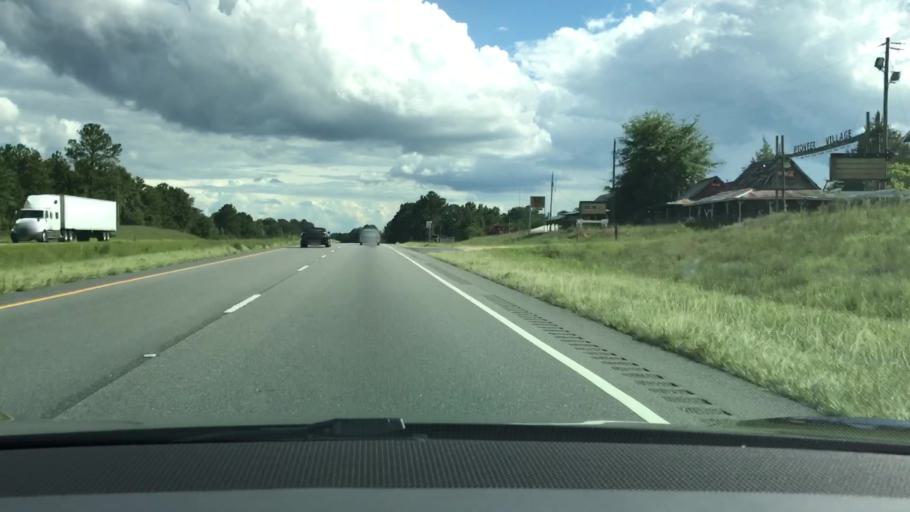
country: US
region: Alabama
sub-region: Pike County
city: Troy
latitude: 31.9021
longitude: -86.0112
